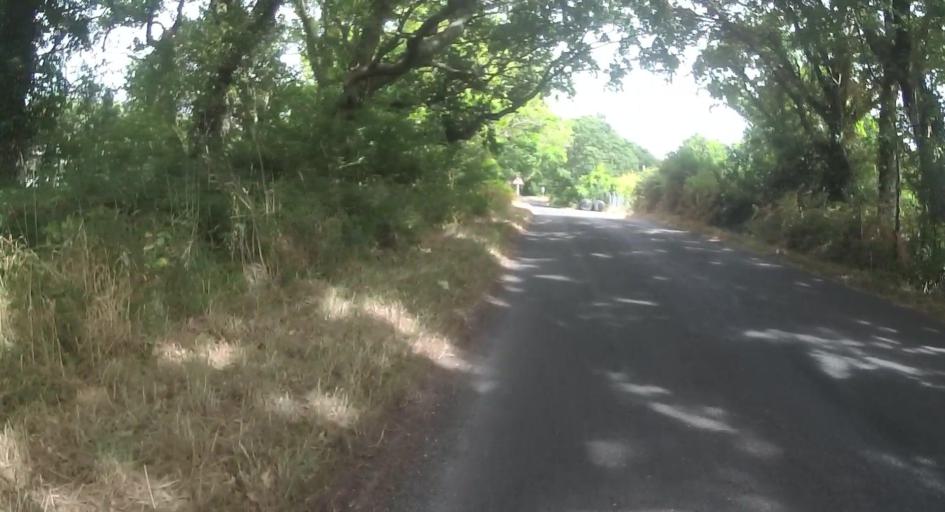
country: GB
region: England
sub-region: Dorset
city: Wool
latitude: 50.6703
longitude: -2.1699
